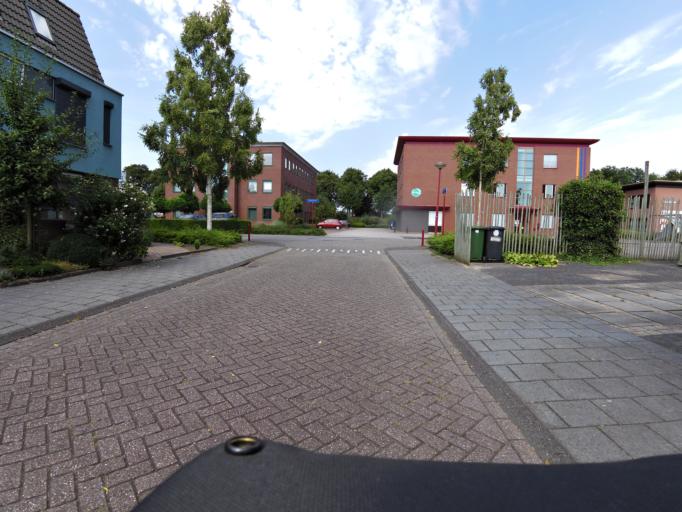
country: NL
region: South Holland
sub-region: Gemeente Oud-Beijerland
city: Oud-Beijerland
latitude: 51.8197
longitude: 4.4386
